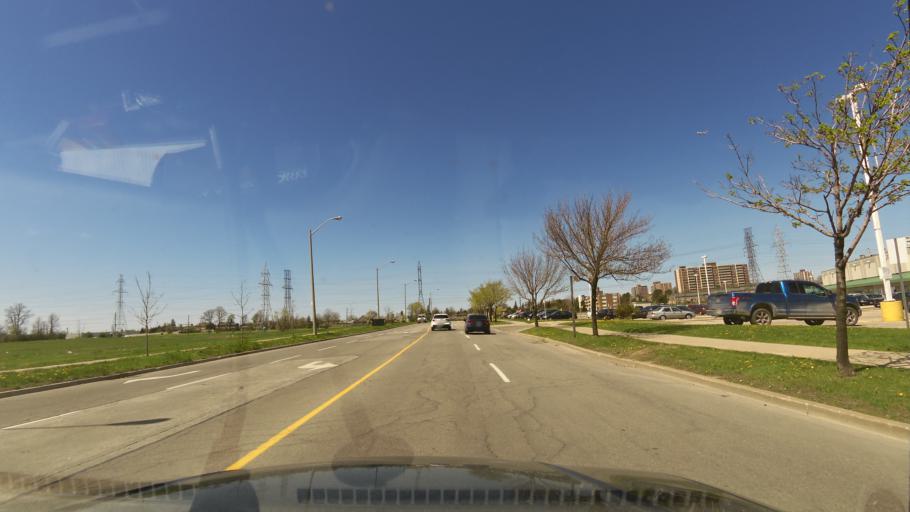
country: CA
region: Ontario
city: Concord
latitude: 43.7573
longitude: -79.5209
